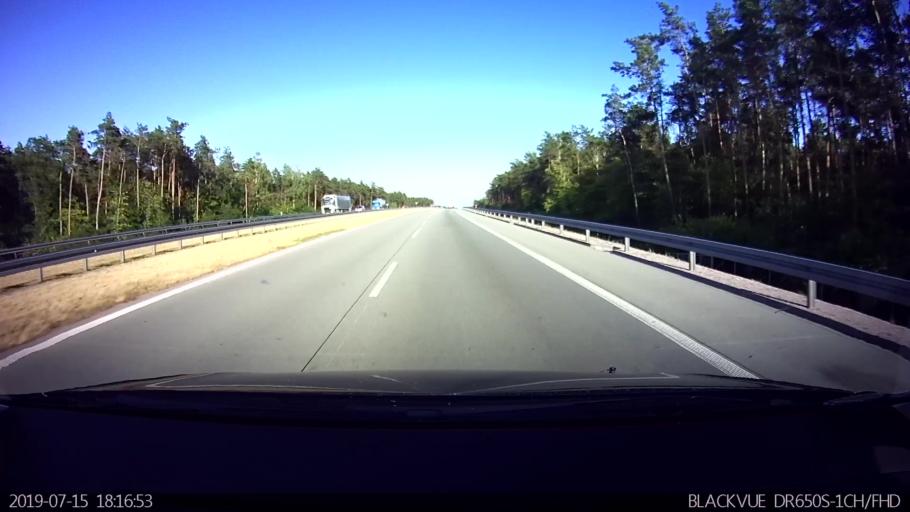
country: PL
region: Lodz Voivodeship
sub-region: Powiat zdunskowolski
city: Zdunska Wola
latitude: 51.5738
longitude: 18.9505
